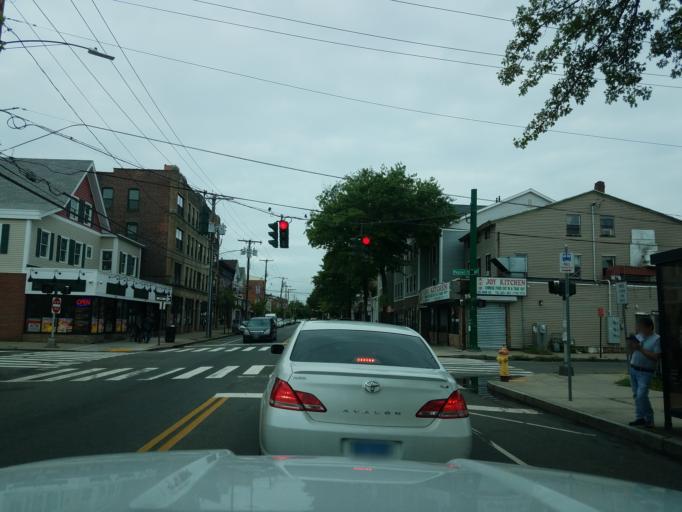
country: US
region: Connecticut
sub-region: New Haven County
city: New Haven
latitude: 41.3089
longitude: -72.8968
